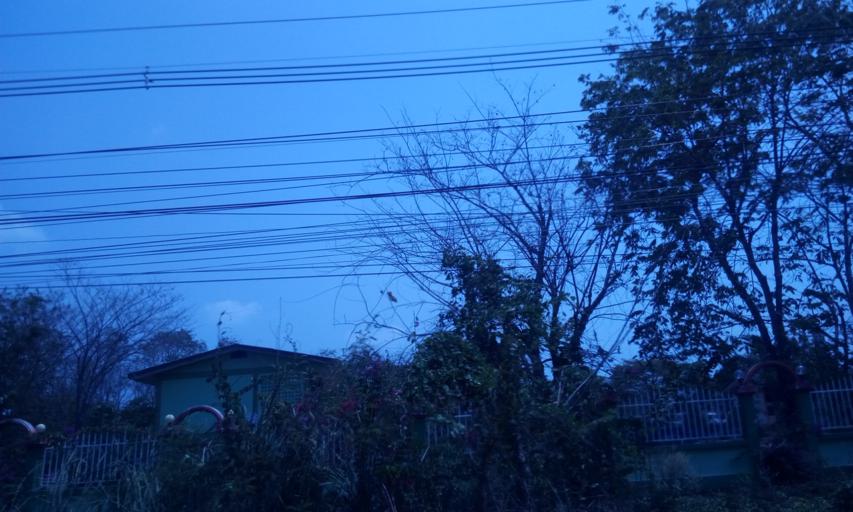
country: TH
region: Chachoengsao
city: Bang Nam Priao
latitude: 13.8011
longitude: 101.0532
